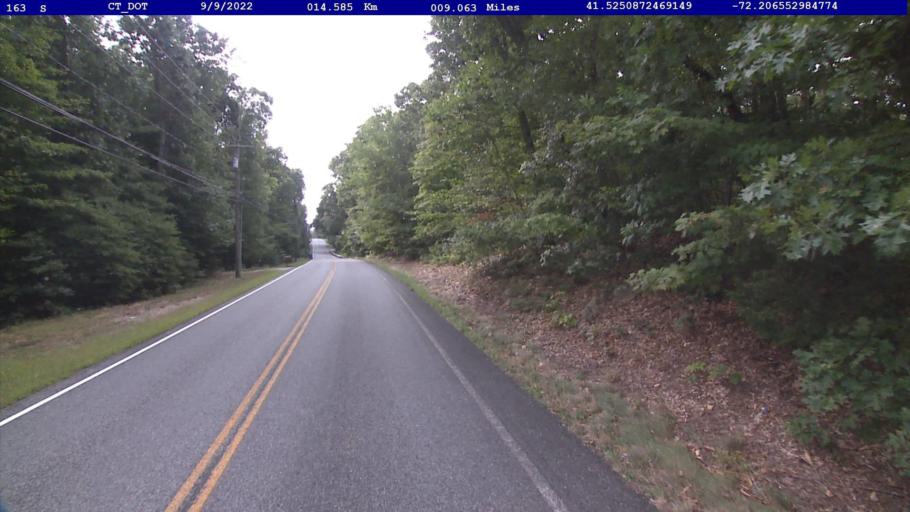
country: US
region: Connecticut
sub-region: New London County
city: Montville Center
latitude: 41.5251
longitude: -72.2065
